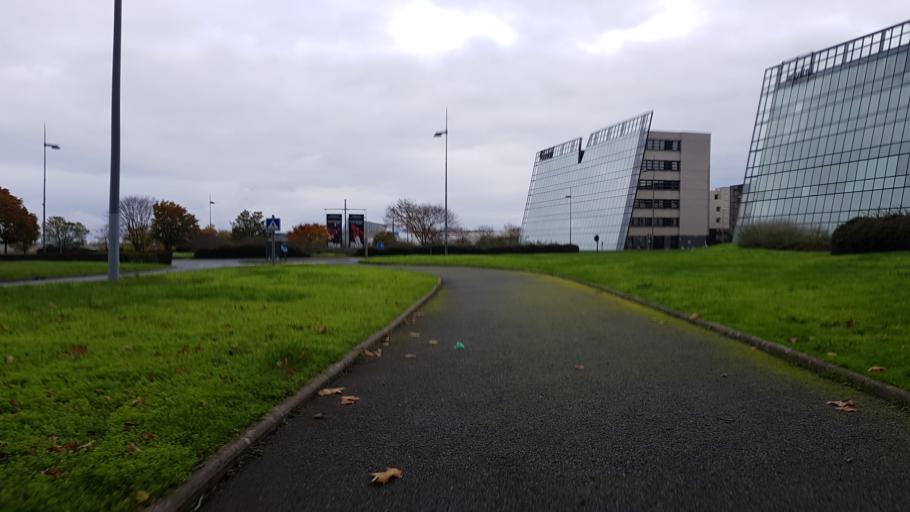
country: FR
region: Poitou-Charentes
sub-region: Departement de la Vienne
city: Chasseneuil-du-Poitou
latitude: 46.6637
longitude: 0.3604
